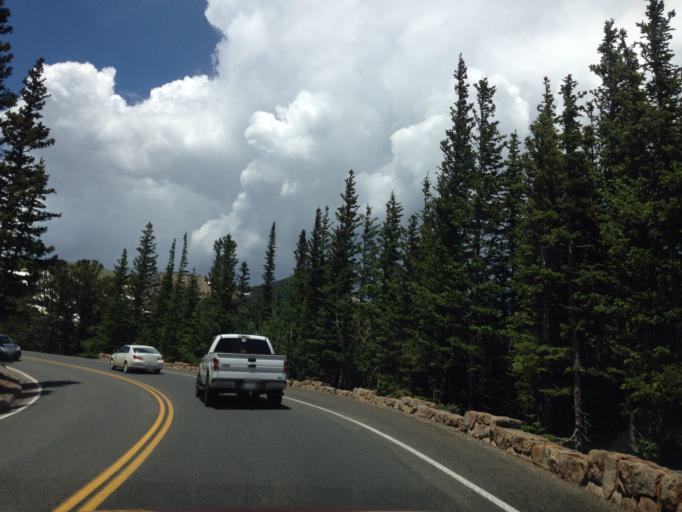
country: US
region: Colorado
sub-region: Larimer County
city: Estes Park
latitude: 40.3867
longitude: -105.6589
